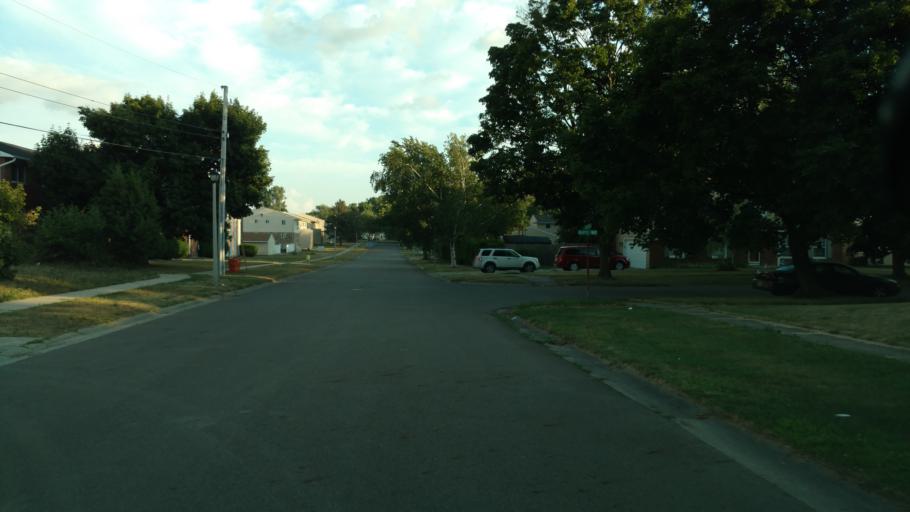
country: US
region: Michigan
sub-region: Eaton County
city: Waverly
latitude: 42.7256
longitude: -84.6072
